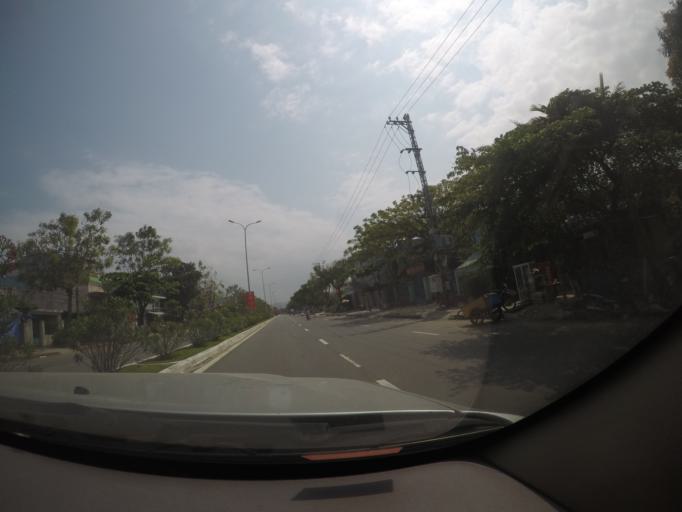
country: VN
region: Da Nang
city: Lien Chieu
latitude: 16.1322
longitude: 108.1195
